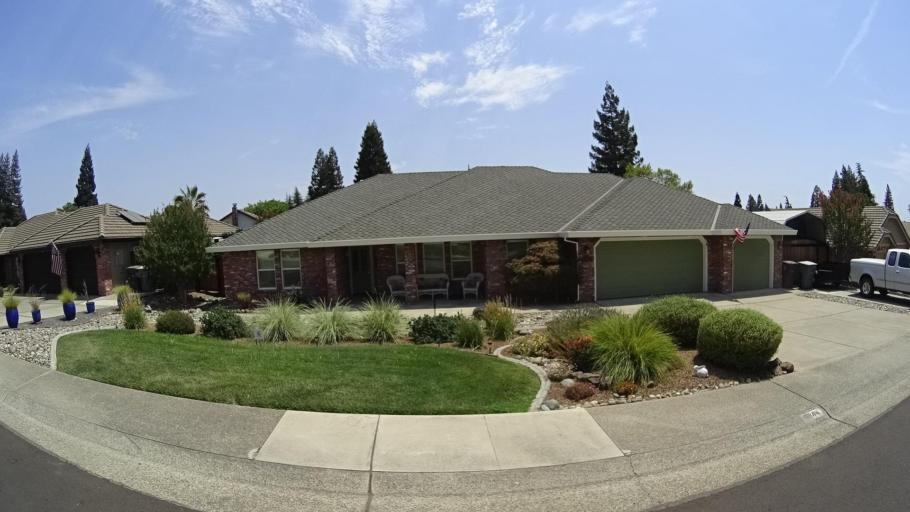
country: US
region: California
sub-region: Placer County
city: Rocklin
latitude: 38.8070
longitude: -121.2307
